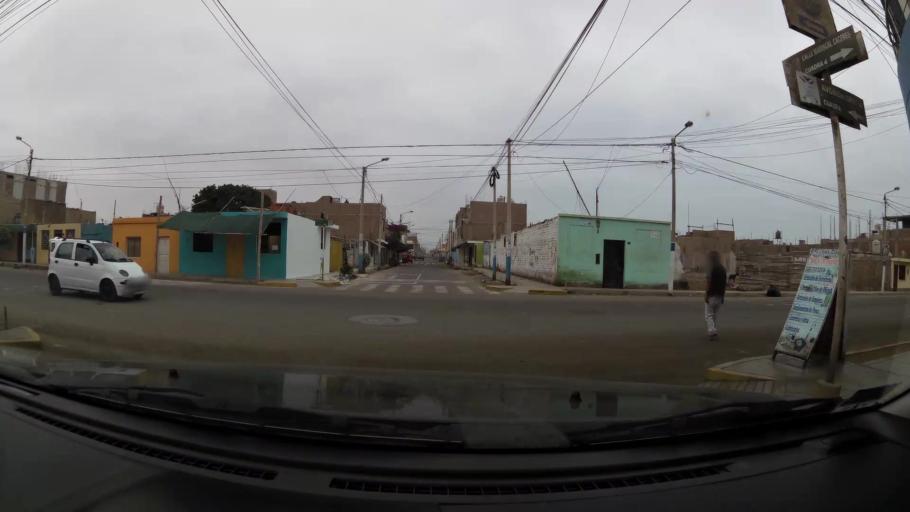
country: PE
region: Ica
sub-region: Provincia de Pisco
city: Pisco
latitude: -13.7322
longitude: -76.2221
